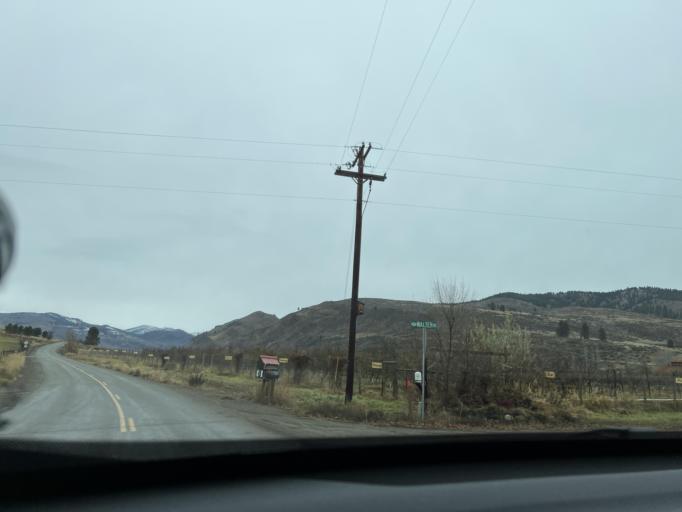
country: US
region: Washington
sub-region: Okanogan County
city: Brewster
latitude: 48.5093
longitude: -120.1730
